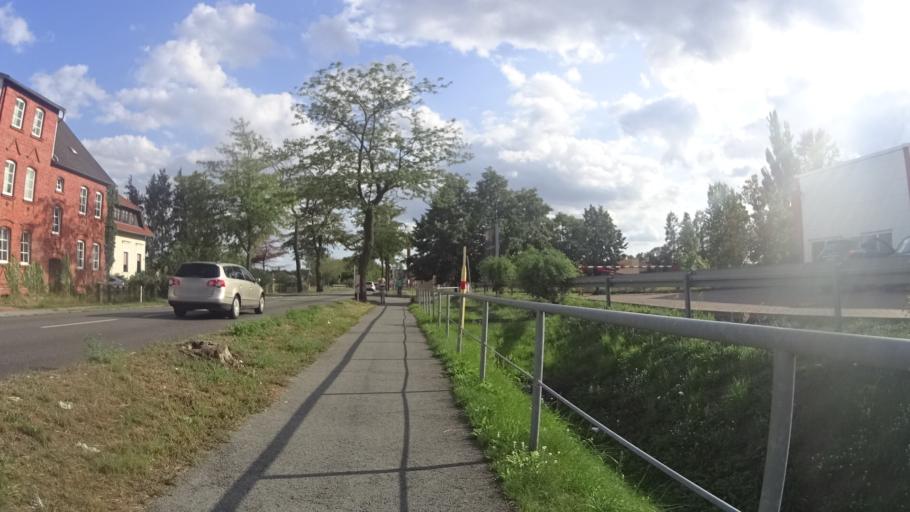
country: DE
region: Brandenburg
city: Rathenow
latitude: 52.5889
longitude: 12.3384
